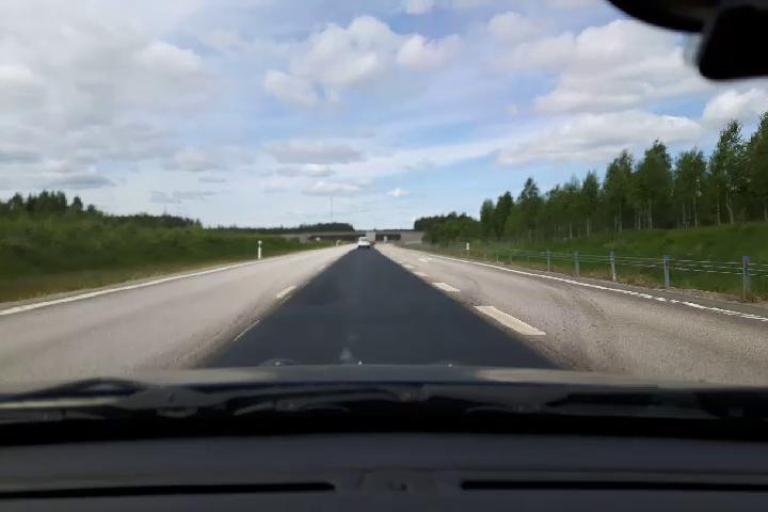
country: SE
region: Uppsala
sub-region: Tierps Kommun
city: Tierp
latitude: 60.4359
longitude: 17.4239
